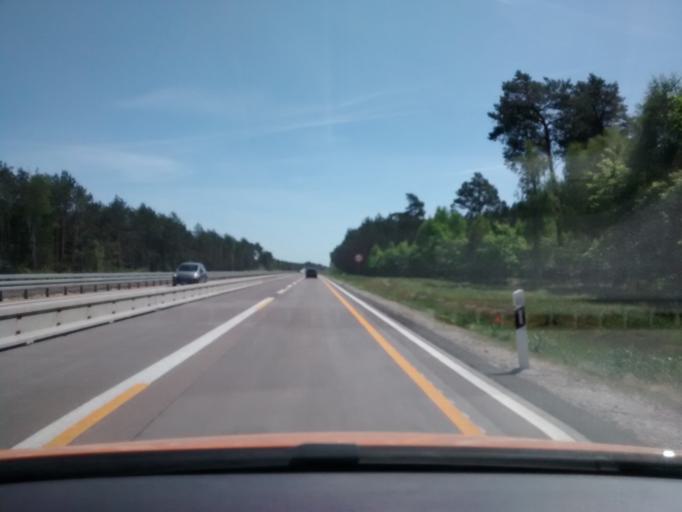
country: DE
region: Brandenburg
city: Erkner
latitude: 52.3190
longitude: 13.7831
